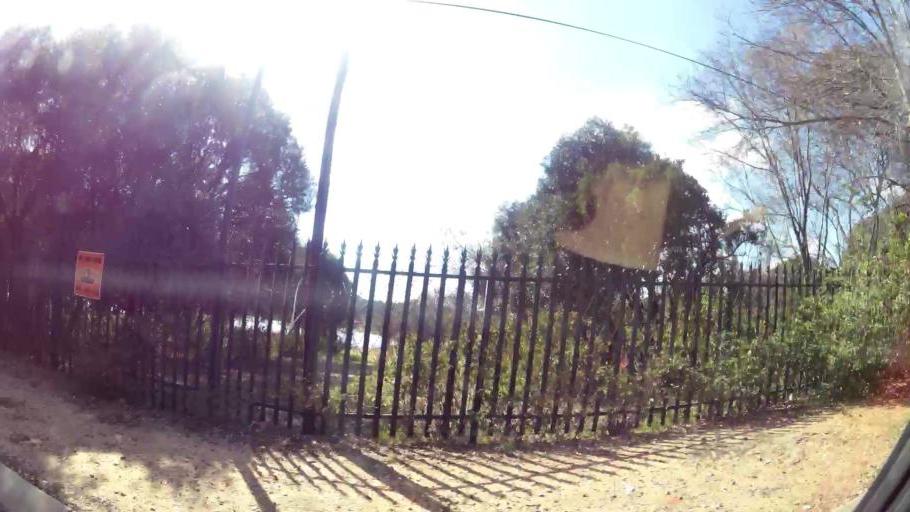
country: ZA
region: Gauteng
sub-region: West Rand District Municipality
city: Muldersdriseloop
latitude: -26.0724
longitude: 27.9541
